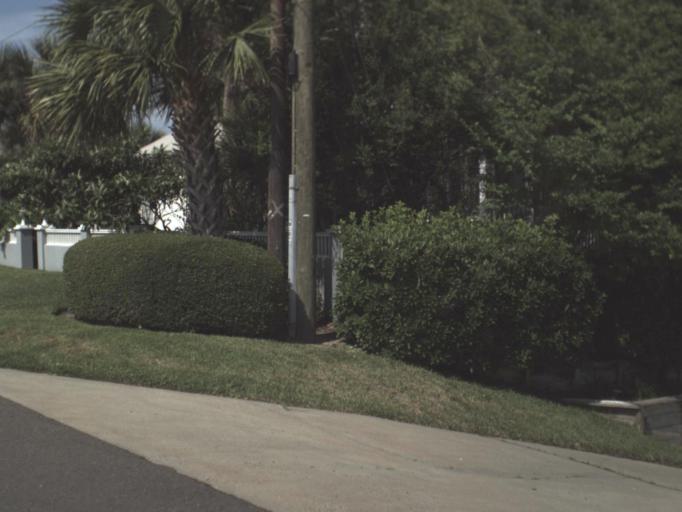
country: US
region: Florida
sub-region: Nassau County
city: Fernandina Beach
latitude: 30.6101
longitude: -81.4425
